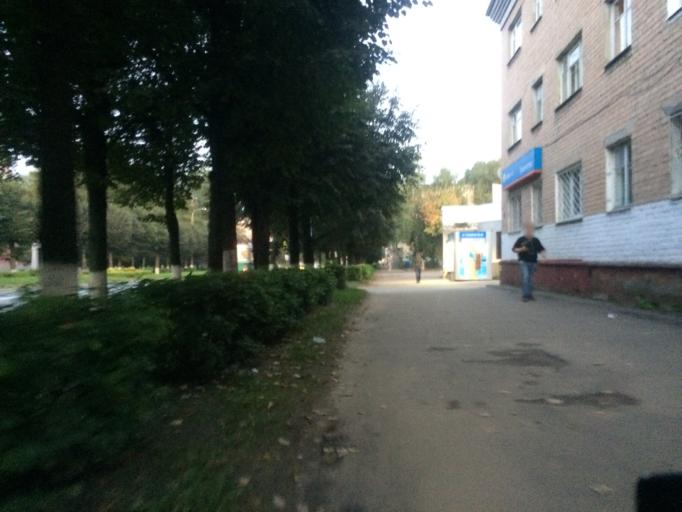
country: RU
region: Mariy-El
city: Yoshkar-Ola
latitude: 56.6361
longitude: 47.8743
